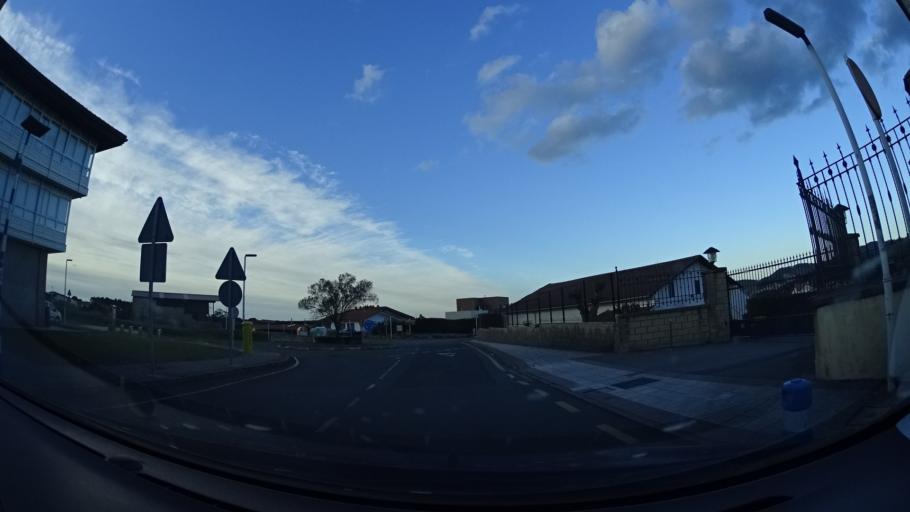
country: ES
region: Basque Country
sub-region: Bizkaia
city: Plentzia
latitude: 43.4061
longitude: -2.9619
